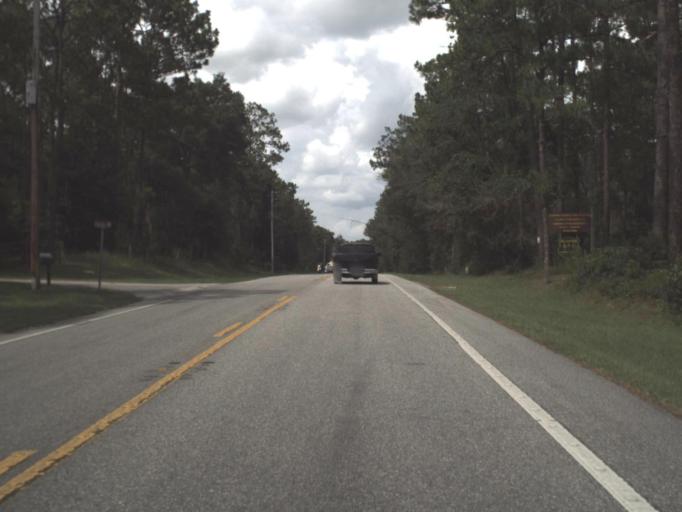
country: US
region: Florida
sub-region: Citrus County
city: Floral City
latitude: 28.6516
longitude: -82.3290
